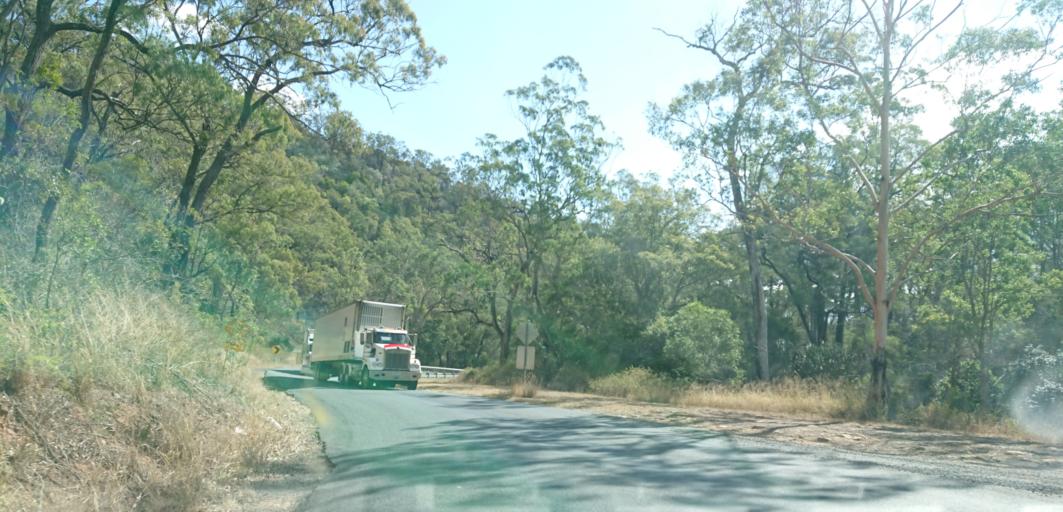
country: AU
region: Queensland
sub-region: Toowoomba
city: Top Camp
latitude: -27.7722
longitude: 152.0908
